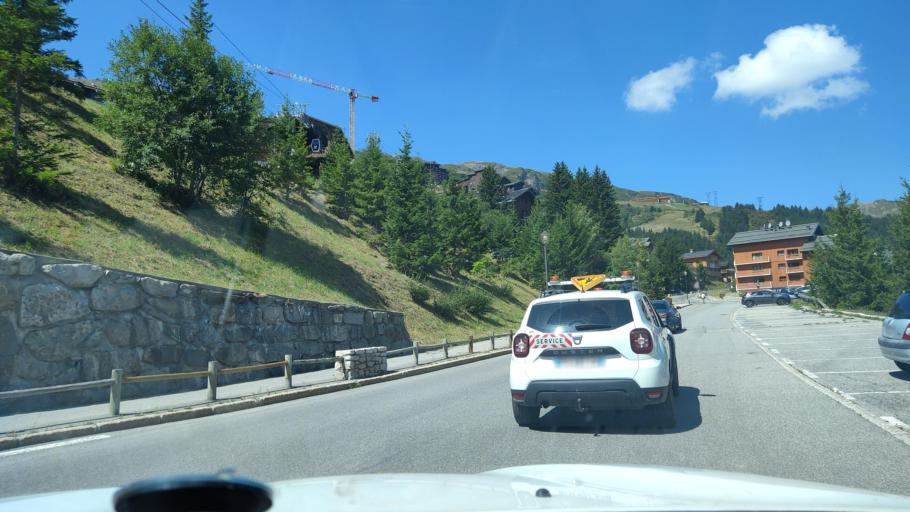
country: FR
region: Rhone-Alpes
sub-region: Departement de la Savoie
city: Meribel
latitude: 45.3743
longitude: 6.5783
